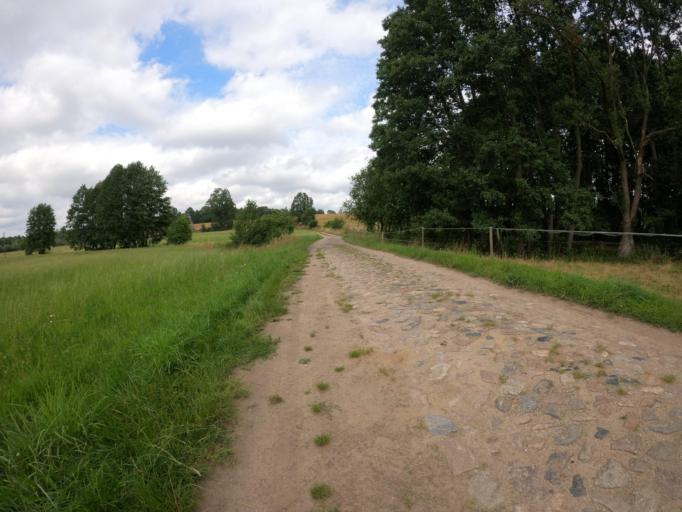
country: PL
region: West Pomeranian Voivodeship
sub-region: Powiat szczecinecki
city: Grzmiaca
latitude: 53.7996
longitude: 16.4732
